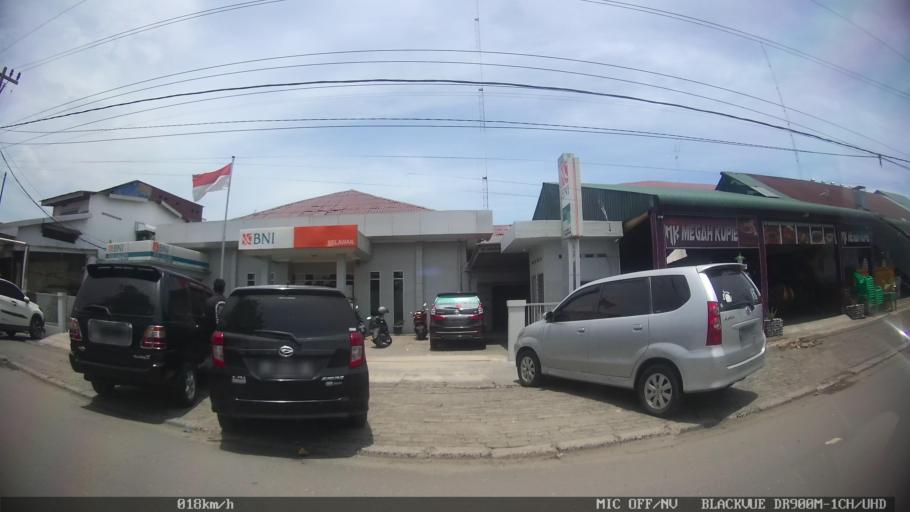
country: ID
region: North Sumatra
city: Belawan
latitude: 3.7836
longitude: 98.6888
